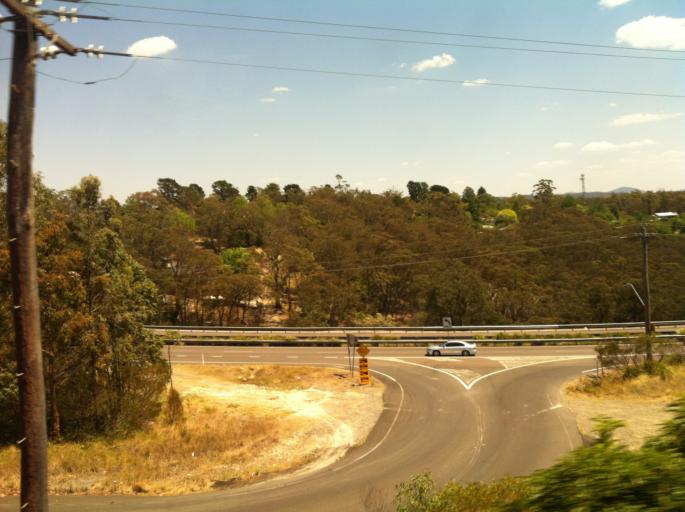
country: AU
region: New South Wales
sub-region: Blue Mountains Municipality
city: Hazelbrook
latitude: -33.7345
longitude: 150.4862
